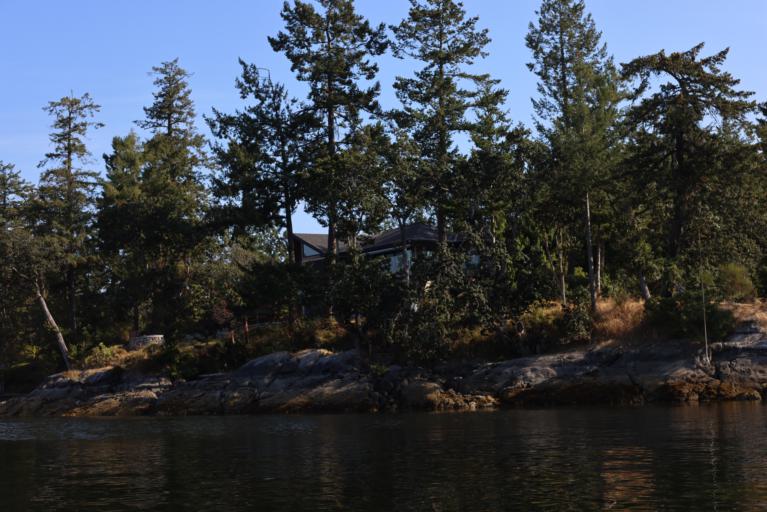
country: CA
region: British Columbia
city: North Saanich
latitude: 48.6811
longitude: -123.4754
